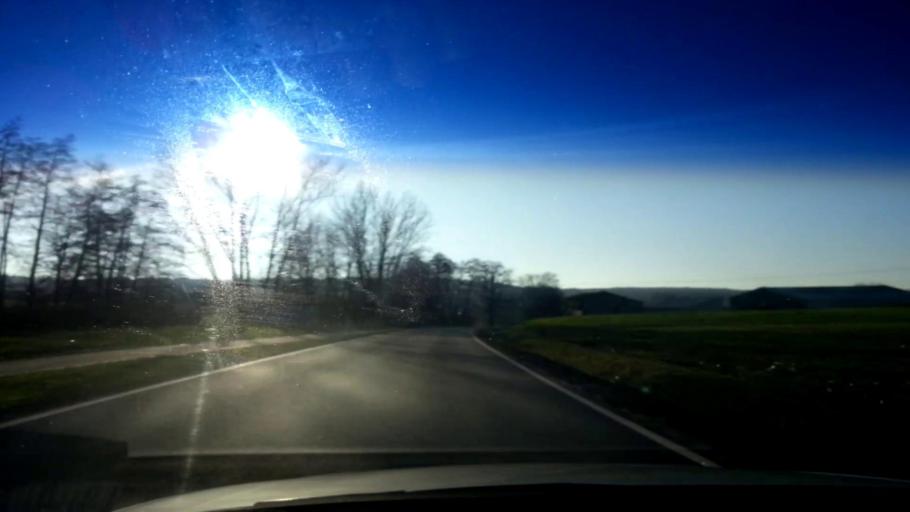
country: DE
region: Bavaria
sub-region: Upper Franconia
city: Litzendorf
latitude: 49.9159
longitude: 10.9971
